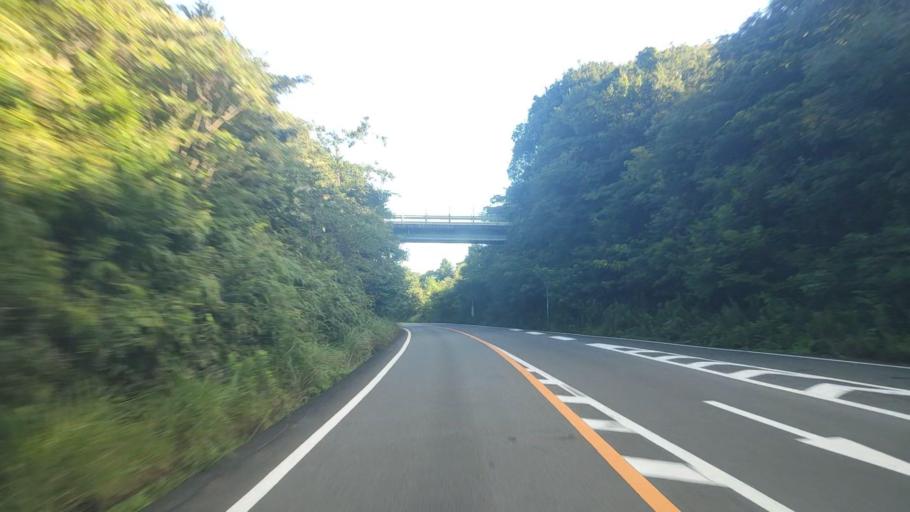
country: JP
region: Mie
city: Toba
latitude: 34.3450
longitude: 136.8394
